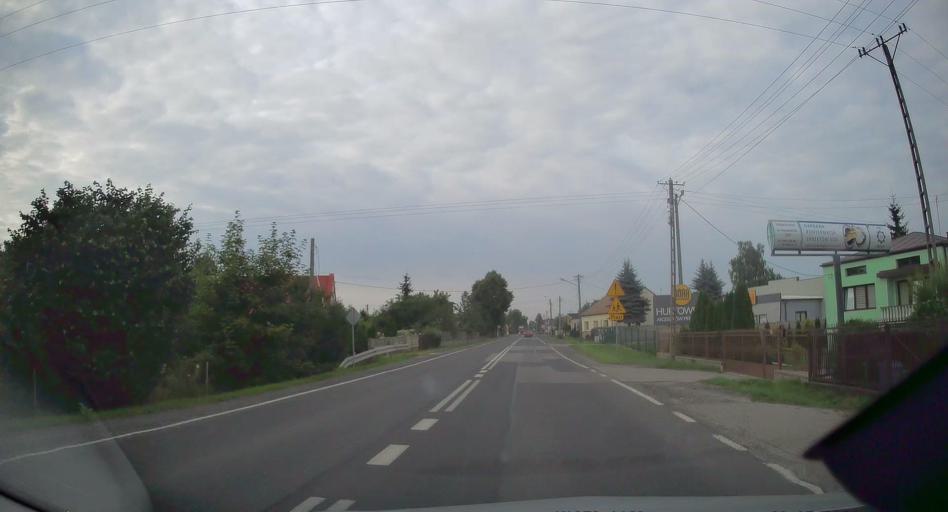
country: PL
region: Lodz Voivodeship
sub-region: Powiat radomszczanski
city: Radomsko
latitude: 51.0926
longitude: 19.4577
